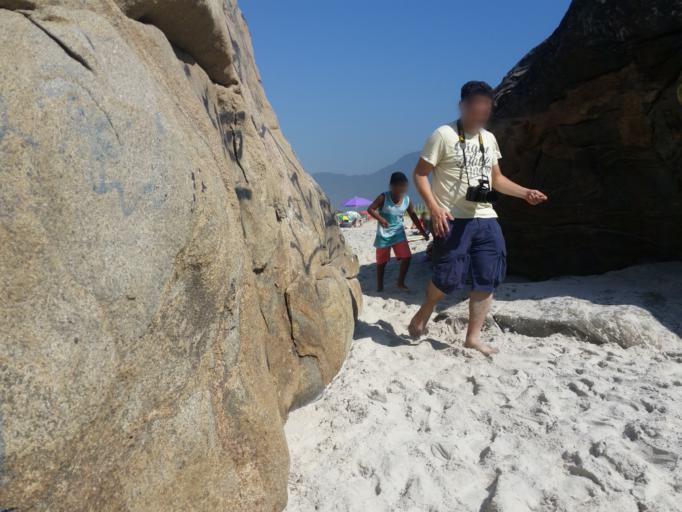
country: BR
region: Rio de Janeiro
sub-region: Nilopolis
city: Nilopolis
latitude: -23.0480
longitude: -43.5164
